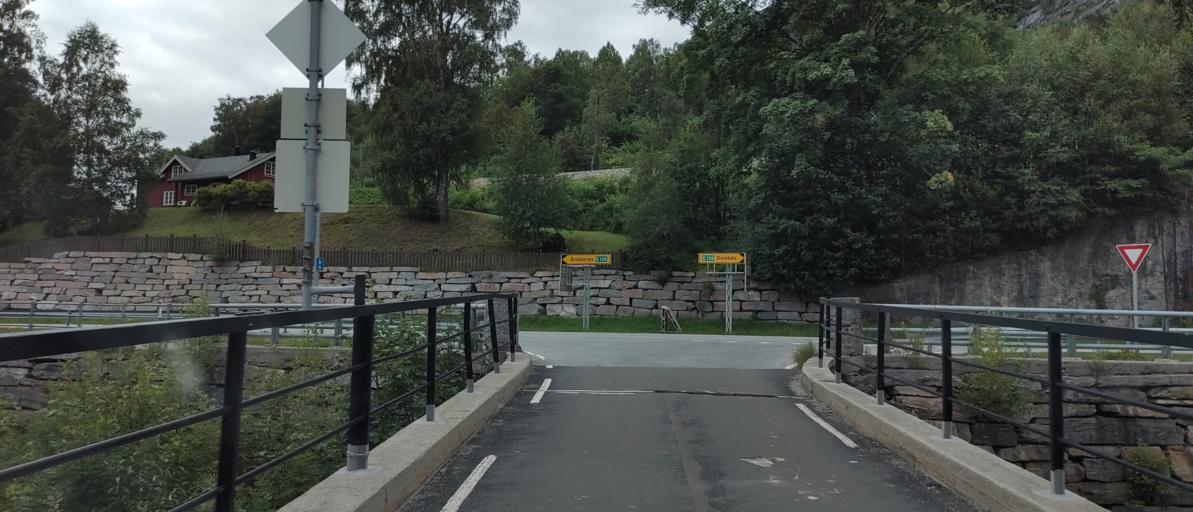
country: NO
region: More og Romsdal
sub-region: Rauma
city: Andalsnes
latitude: 62.5328
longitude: 7.7368
